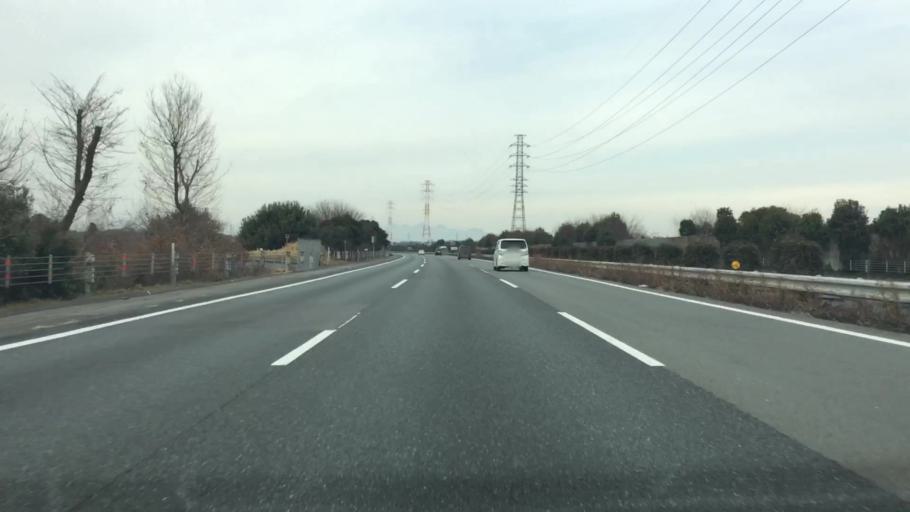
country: JP
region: Saitama
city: Yorii
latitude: 36.1548
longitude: 139.2165
